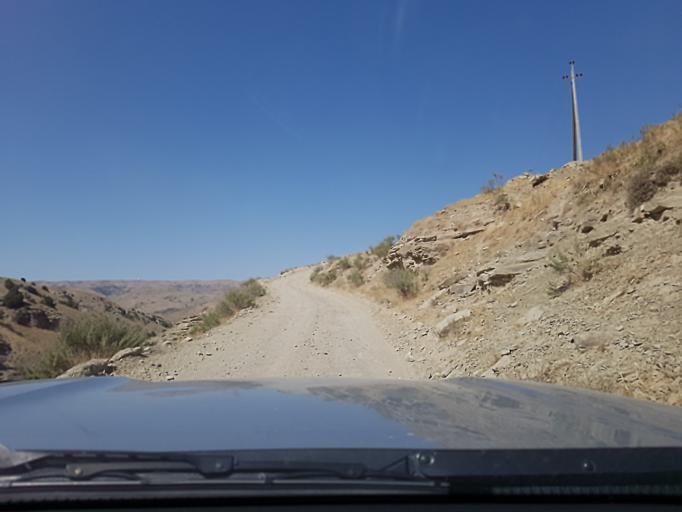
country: TM
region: Ahal
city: Baharly
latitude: 38.3839
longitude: 56.9165
